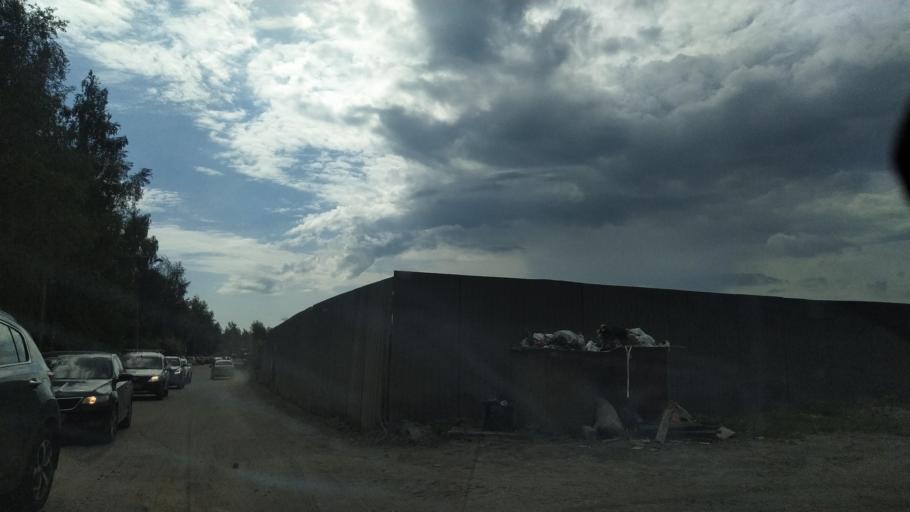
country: RU
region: St.-Petersburg
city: Aleksandrovskaya
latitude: 59.7639
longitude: 30.2639
